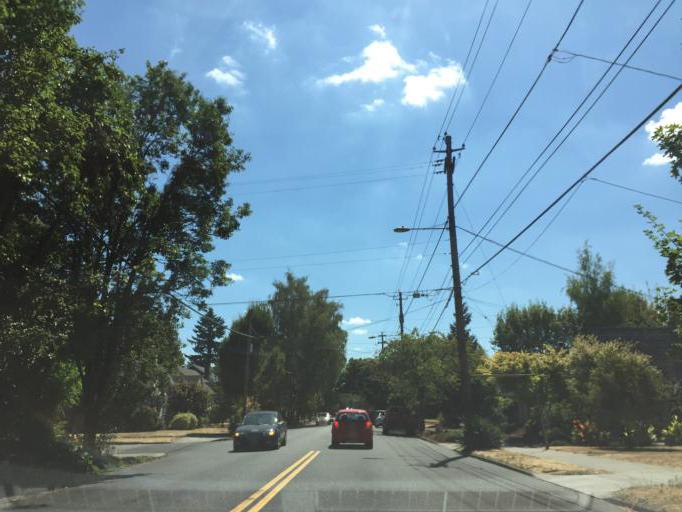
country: US
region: Oregon
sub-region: Multnomah County
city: Portland
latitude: 45.5450
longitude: -122.6307
